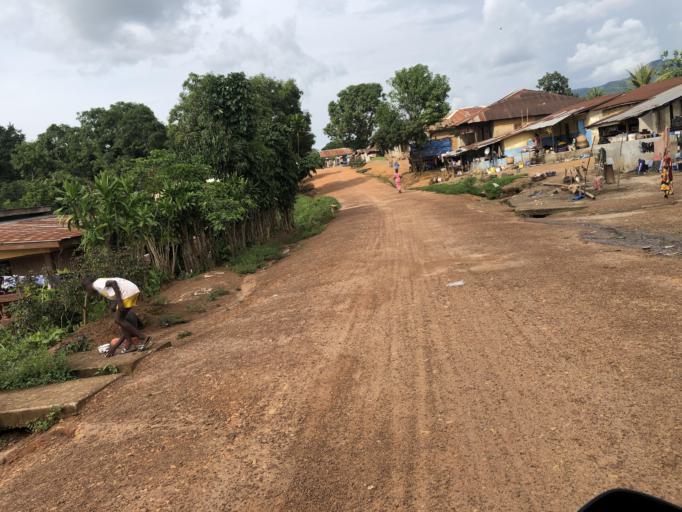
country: SL
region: Northern Province
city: Masaka
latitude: 8.7480
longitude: -11.8408
